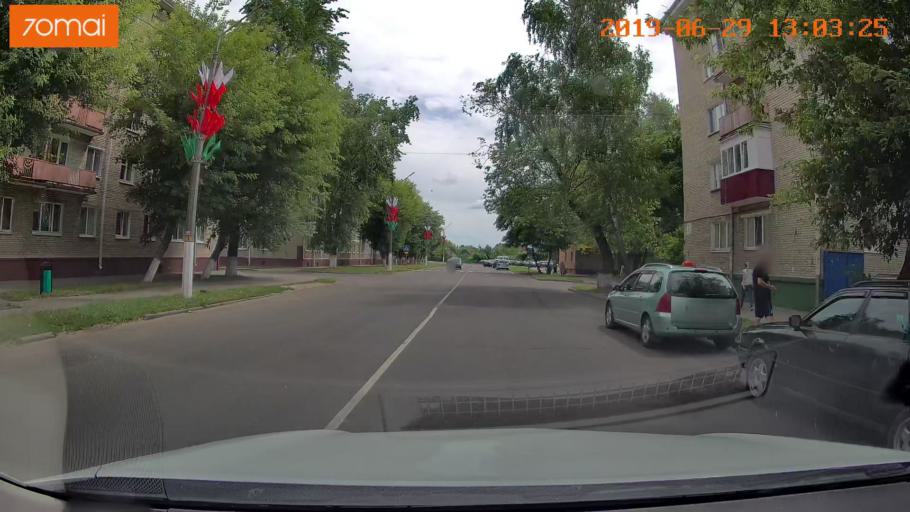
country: BY
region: Minsk
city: Slutsk
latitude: 53.0322
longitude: 27.5612
